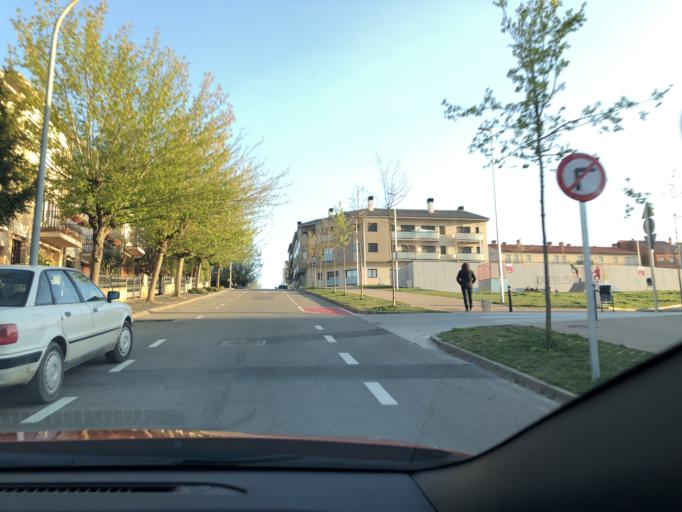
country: ES
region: Catalonia
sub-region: Provincia de Lleida
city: Solsona
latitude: 41.9918
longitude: 1.5151
